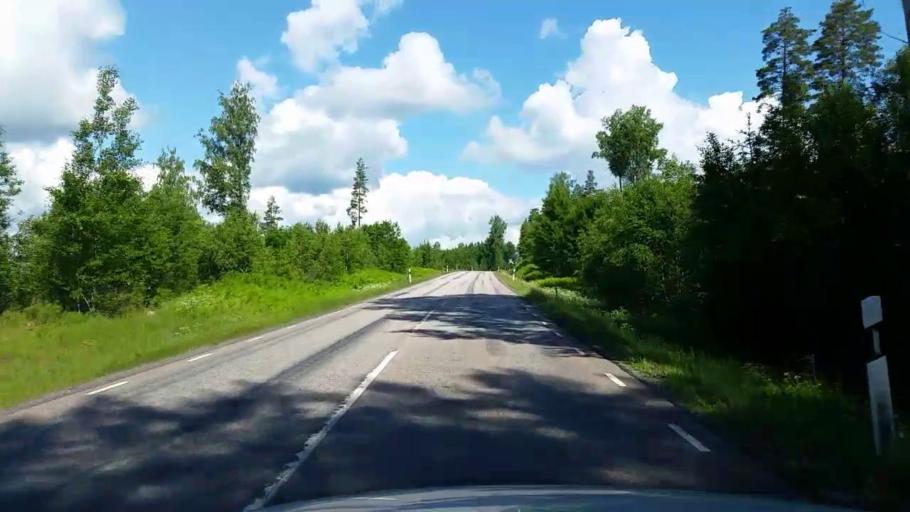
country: SE
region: Vaestmanland
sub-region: Kopings Kommun
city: Kolsva
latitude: 59.6358
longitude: 15.7978
